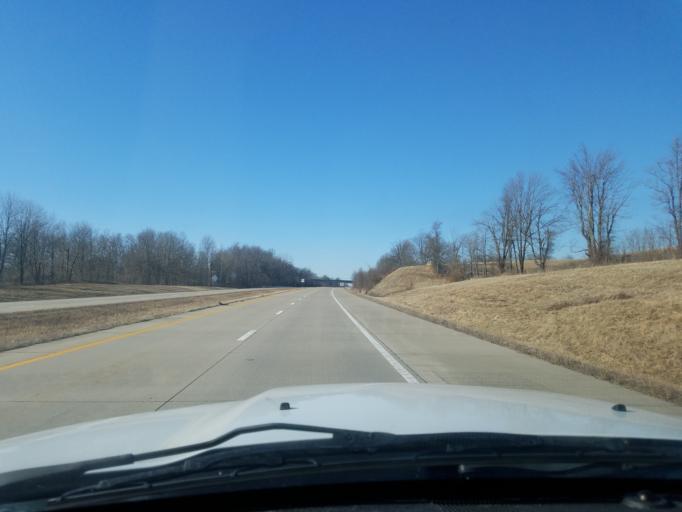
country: US
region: Indiana
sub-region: Warrick County
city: Newburgh
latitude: 37.7571
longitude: -87.4109
